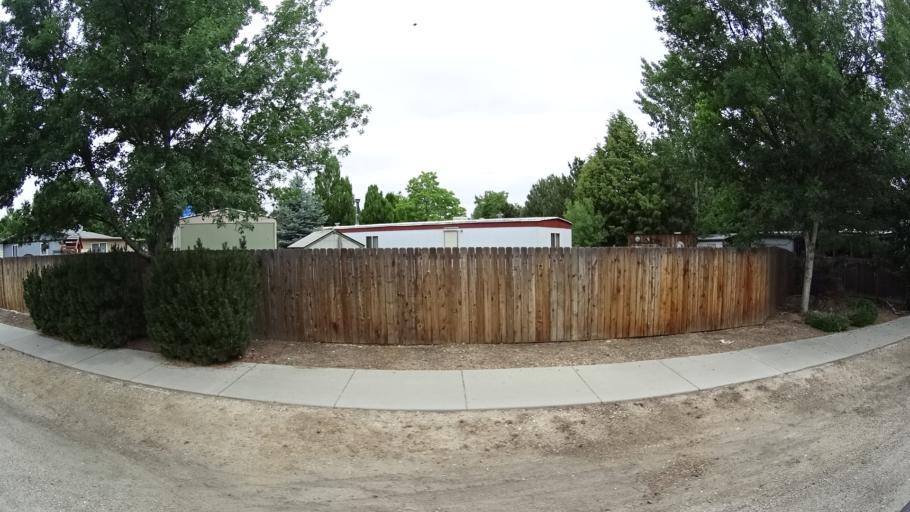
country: US
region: Idaho
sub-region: Ada County
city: Boise
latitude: 43.5754
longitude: -116.2088
